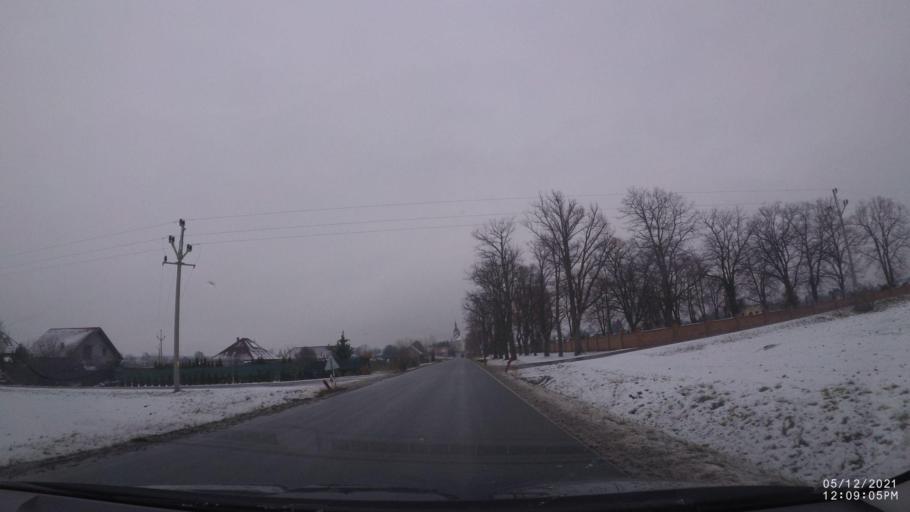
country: CZ
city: Ceske Mezirici
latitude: 50.2857
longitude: 16.0368
